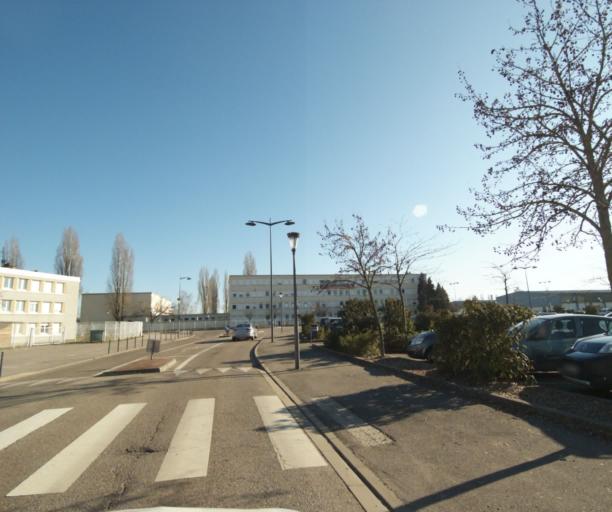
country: FR
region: Lorraine
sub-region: Departement de Meurthe-et-Moselle
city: Saint-Max
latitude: 48.6971
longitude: 6.2155
